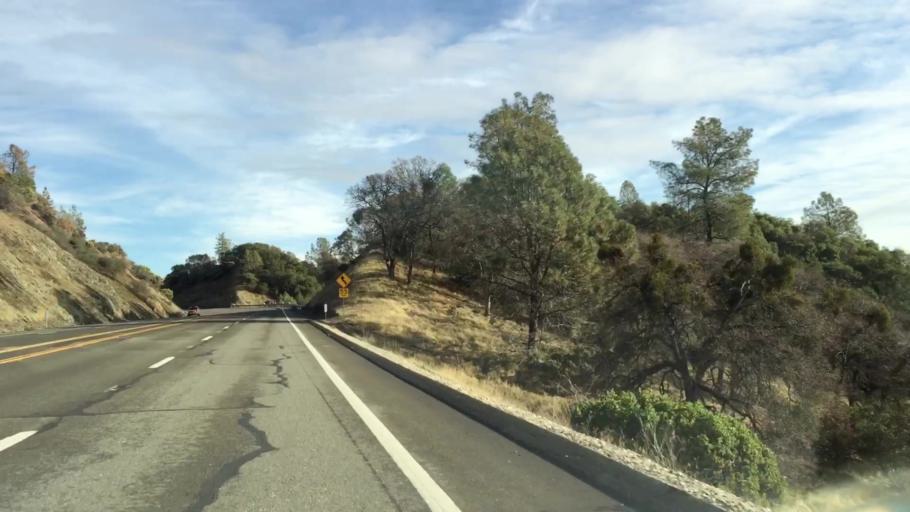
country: US
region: California
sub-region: Butte County
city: Paradise
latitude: 39.6877
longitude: -121.5371
